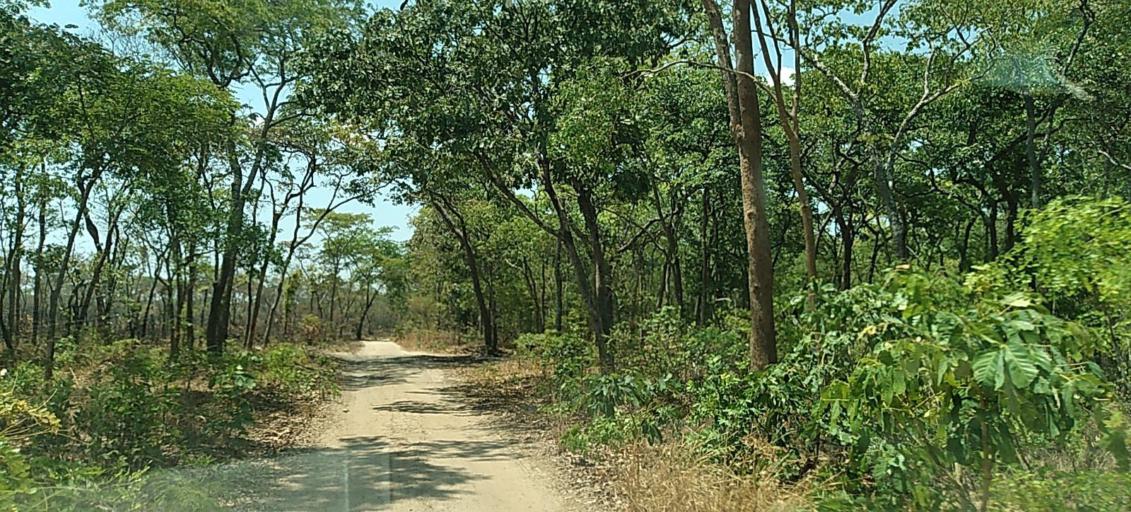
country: ZM
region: Copperbelt
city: Mpongwe
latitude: -13.6416
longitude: 28.4837
